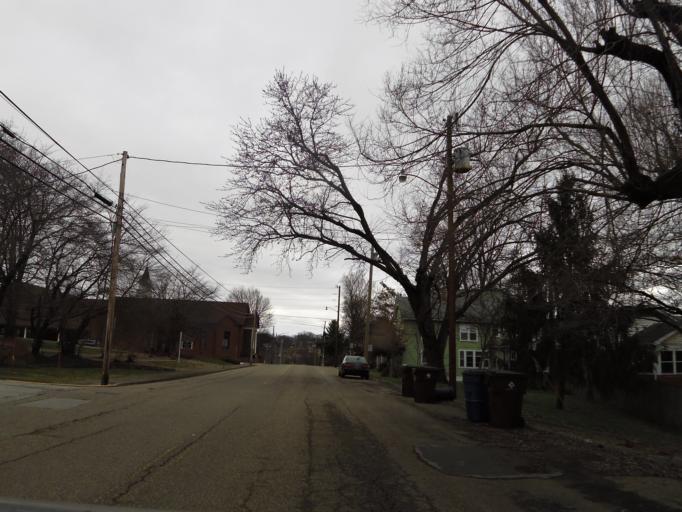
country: US
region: Tennessee
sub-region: Jefferson County
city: Jefferson City
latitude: 36.1243
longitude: -83.4898
